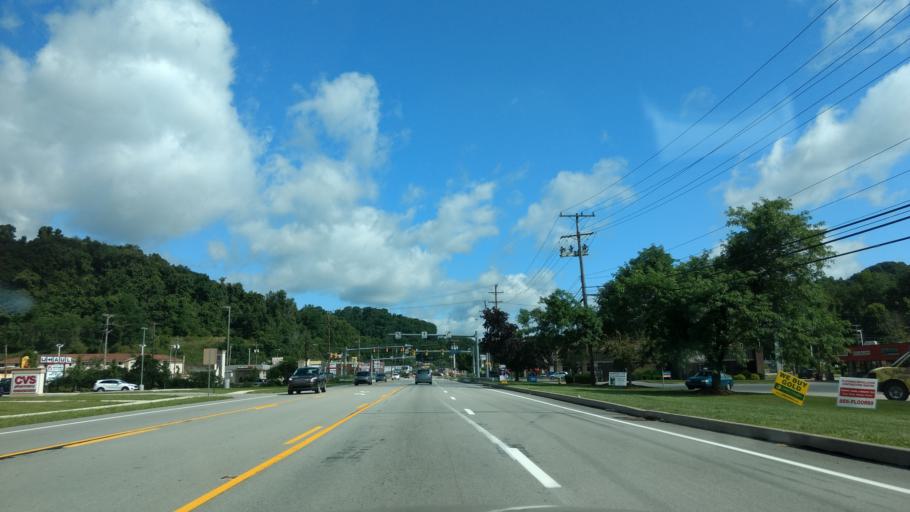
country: US
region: Pennsylvania
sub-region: Westmoreland County
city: Murrysville
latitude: 40.4445
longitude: -79.7136
